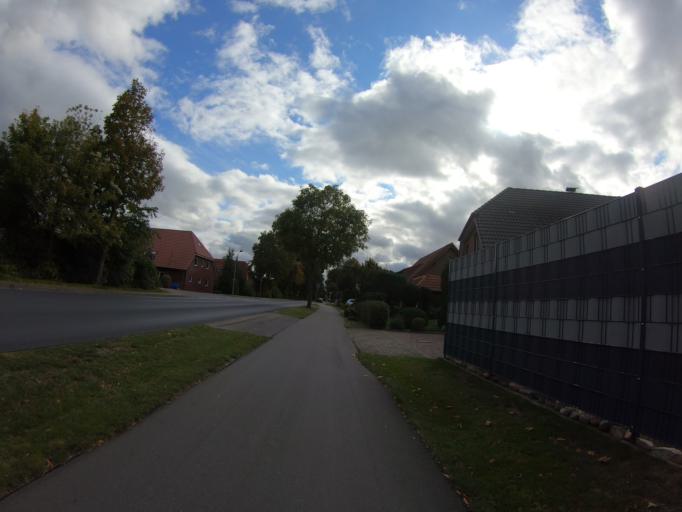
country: DE
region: Lower Saxony
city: Wasbuttel
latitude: 52.4177
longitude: 10.5906
